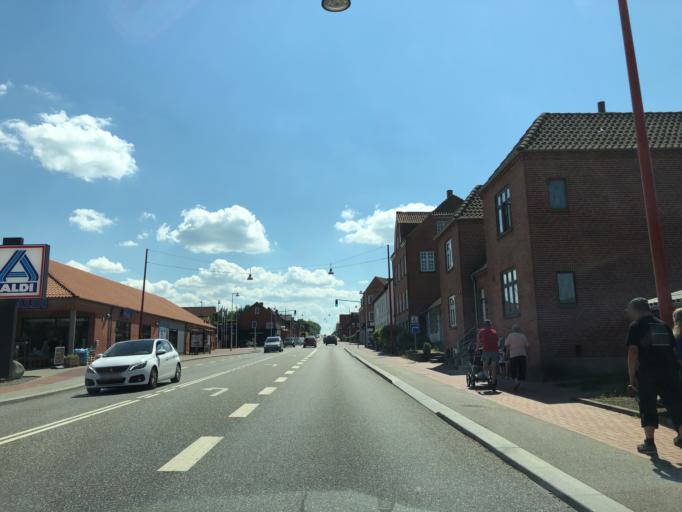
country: DK
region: Central Jutland
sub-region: Struer Kommune
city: Struer
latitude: 56.4920
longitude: 8.5838
